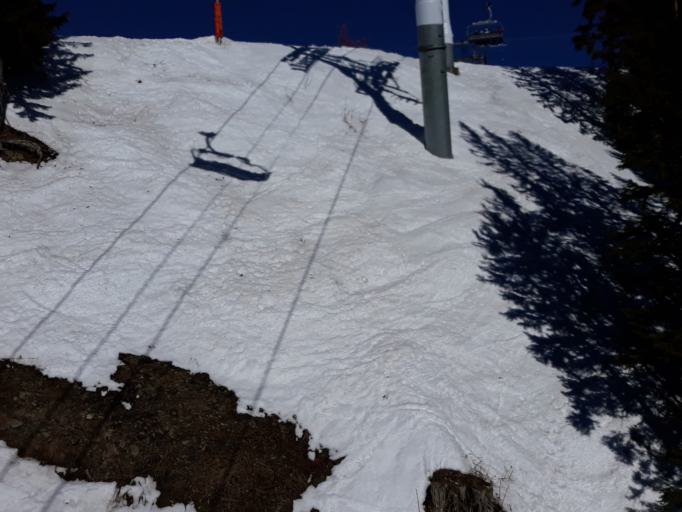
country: FR
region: Rhone-Alpes
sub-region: Departement de la Haute-Savoie
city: Araches-la-Frasse
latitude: 46.0333
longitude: 6.6763
